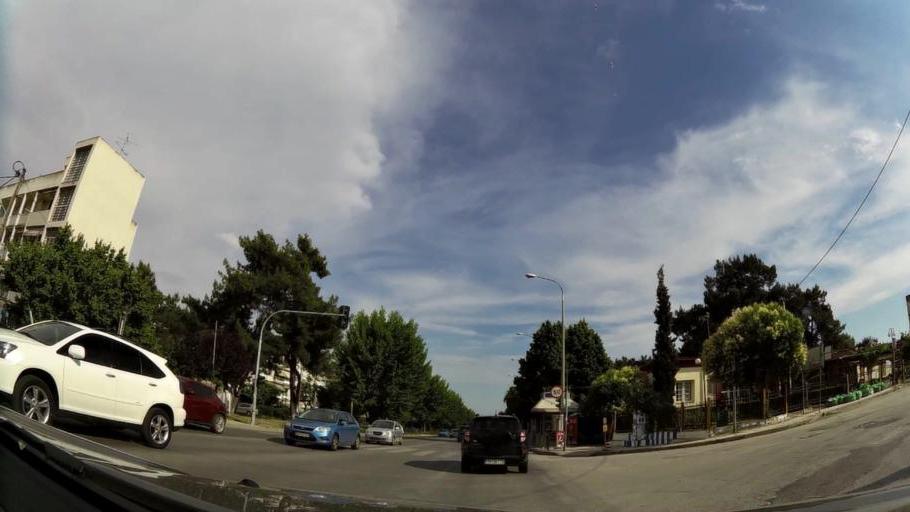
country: GR
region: Central Macedonia
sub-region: Nomos Thessalonikis
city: Kalamaria
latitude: 40.5729
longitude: 22.9716
